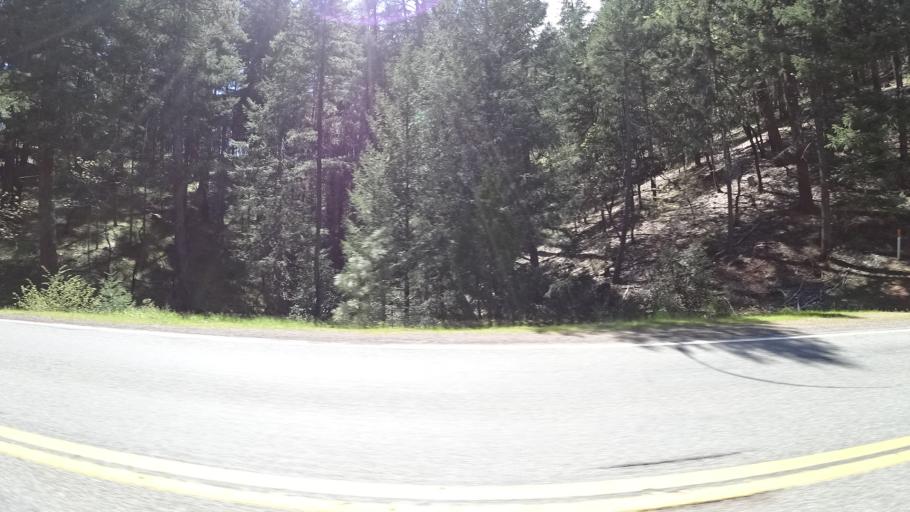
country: US
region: California
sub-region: Trinity County
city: Weaverville
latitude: 40.7920
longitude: -122.8935
